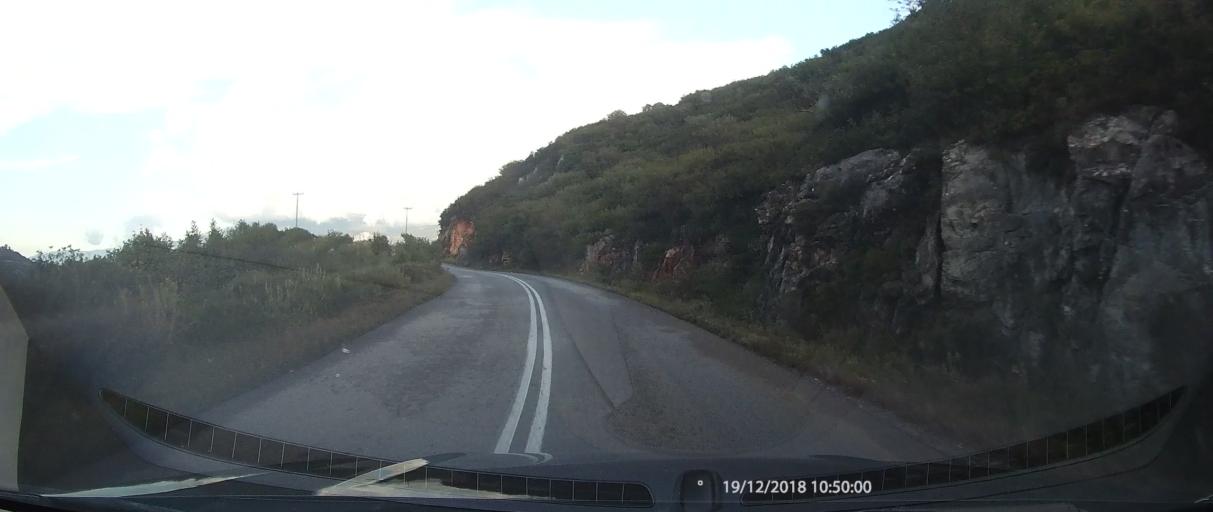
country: GR
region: Peloponnese
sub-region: Nomos Messinias
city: Kardamyli
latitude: 36.9230
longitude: 22.2038
